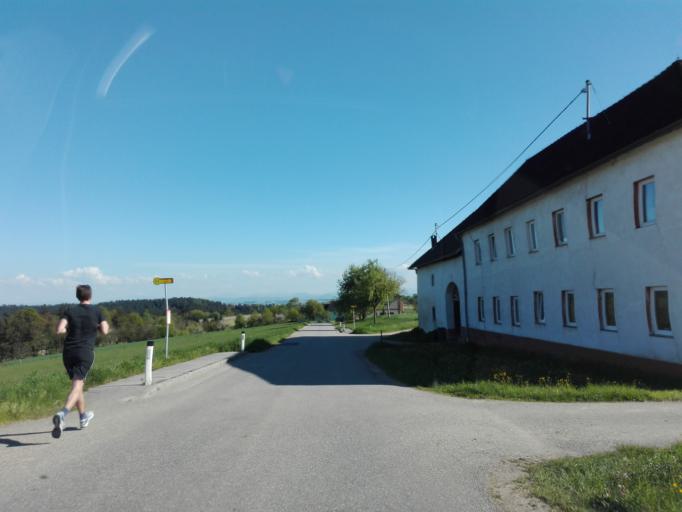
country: AT
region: Upper Austria
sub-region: Politischer Bezirk Perg
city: Perg
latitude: 48.2558
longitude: 14.6790
